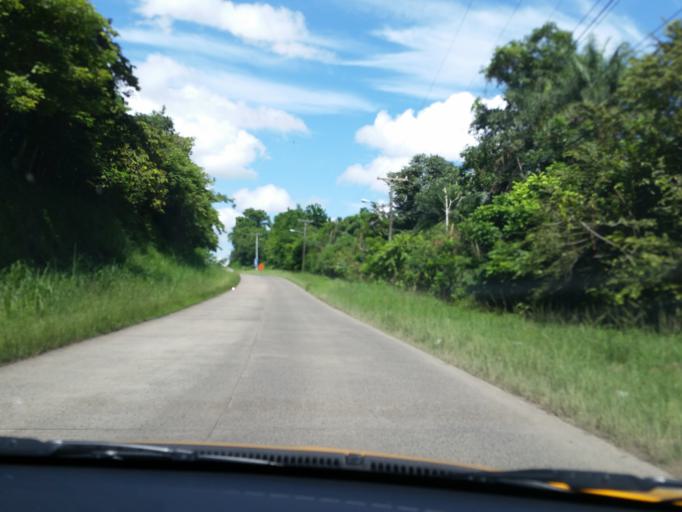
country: PA
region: Panama
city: San Miguelito
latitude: 9.0722
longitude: -79.4669
